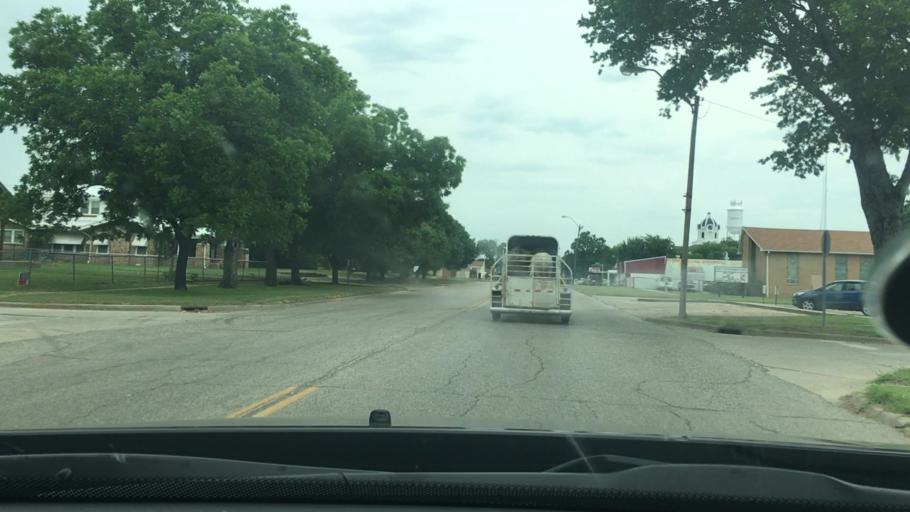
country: US
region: Oklahoma
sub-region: Love County
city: Marietta
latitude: 33.9377
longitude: -97.1242
